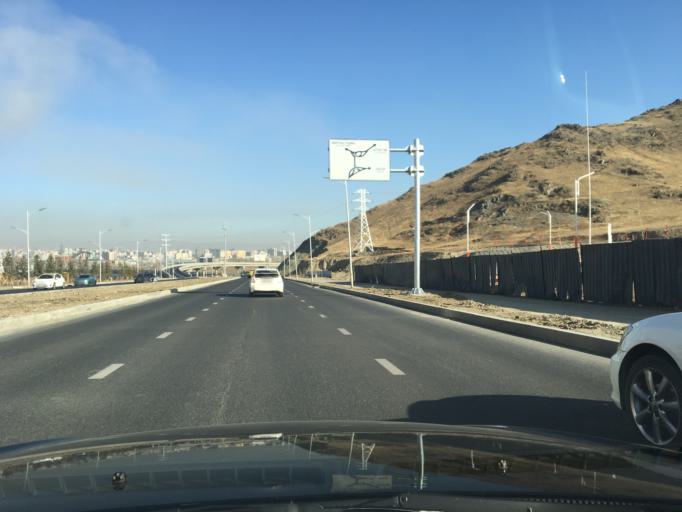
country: MN
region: Ulaanbaatar
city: Ulaanbaatar
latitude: 47.8827
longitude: 106.8608
